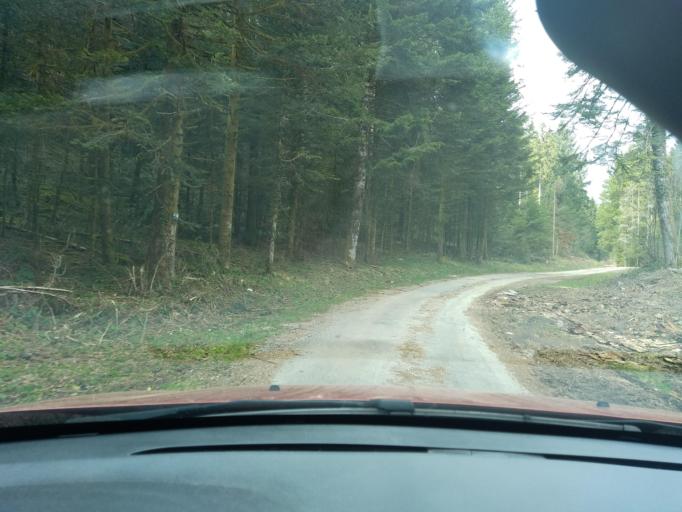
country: FR
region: Franche-Comte
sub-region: Departement du Jura
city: Moirans-en-Montagne
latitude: 46.4727
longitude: 5.7529
